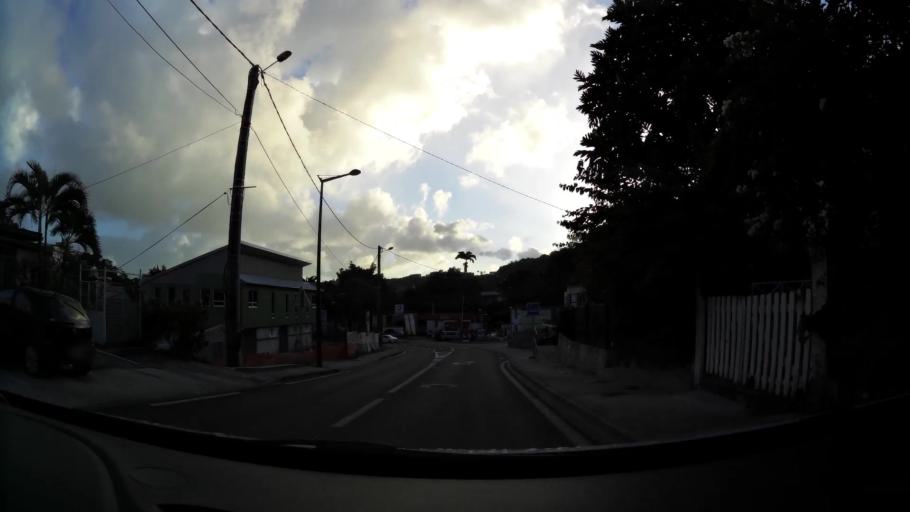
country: MQ
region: Martinique
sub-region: Martinique
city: Fort-de-France
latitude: 14.6185
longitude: -61.0708
